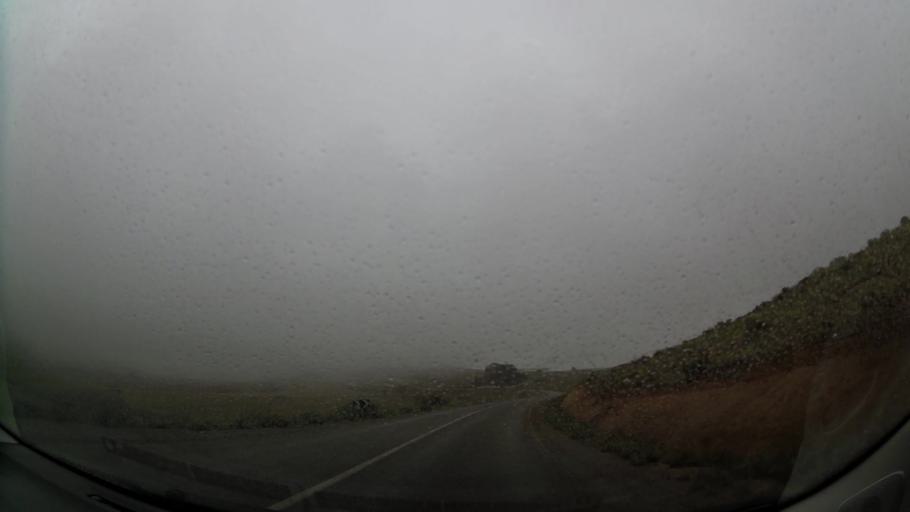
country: MA
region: Oriental
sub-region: Nador
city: Boudinar
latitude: 35.1353
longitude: -3.5989
